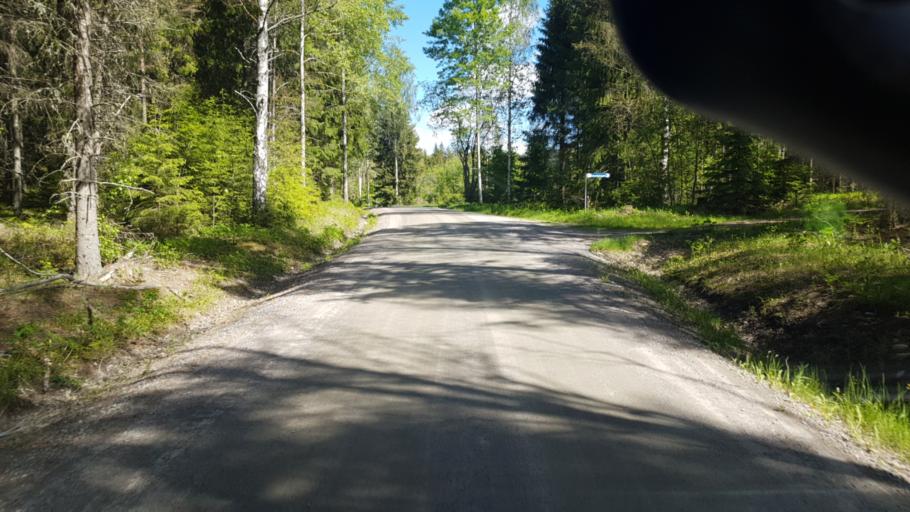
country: SE
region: Vaermland
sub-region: Grums Kommun
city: Slottsbron
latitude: 59.4601
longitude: 12.9184
